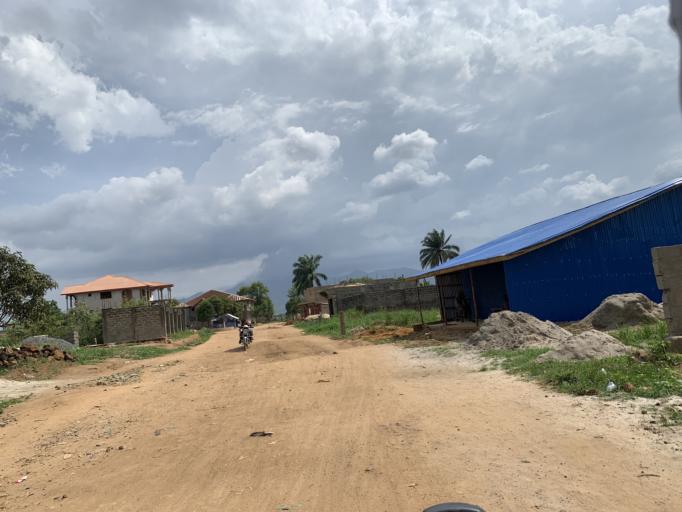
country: SL
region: Western Area
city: Waterloo
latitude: 8.3474
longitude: -13.0513
